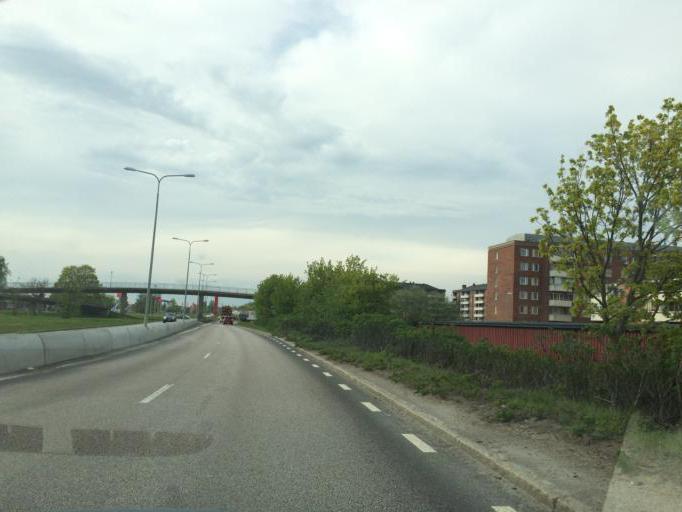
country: SE
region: Vaestmanland
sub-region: Kopings Kommun
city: Koping
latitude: 59.5098
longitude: 15.9913
